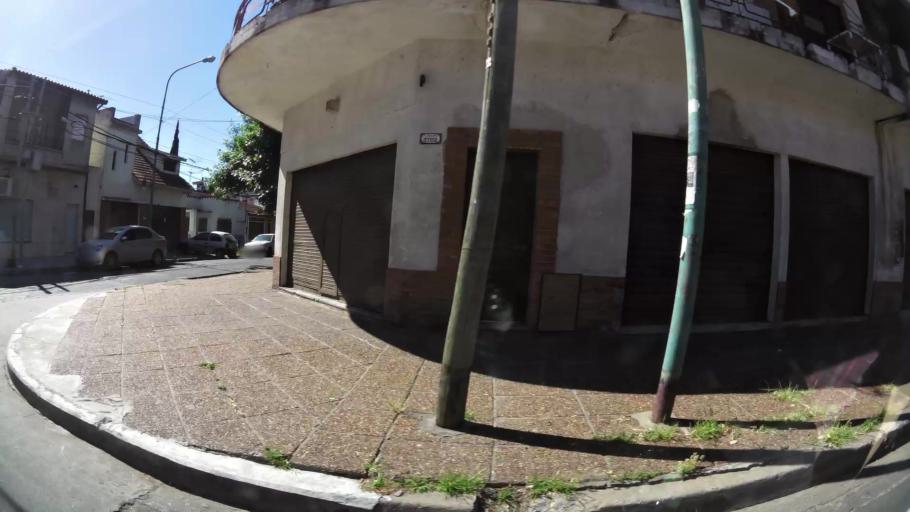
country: AR
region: Buenos Aires
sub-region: Partido de Vicente Lopez
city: Olivos
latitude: -34.5277
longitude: -58.5120
